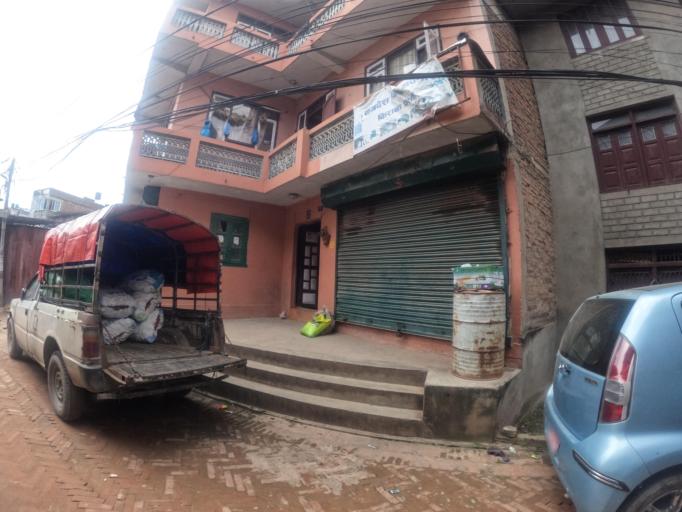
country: NP
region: Central Region
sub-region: Bagmati Zone
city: Bhaktapur
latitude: 27.6860
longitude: 85.3856
